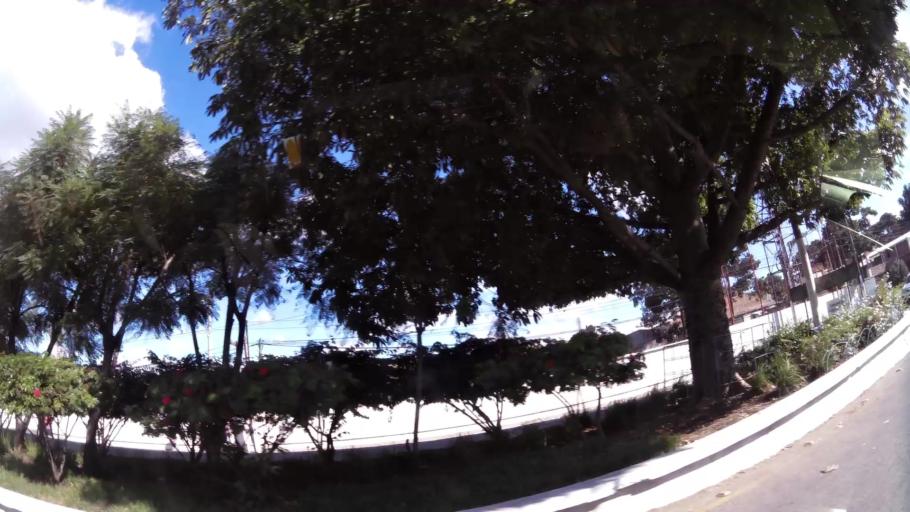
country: GT
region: Guatemala
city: Villa Nueva
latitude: 14.5314
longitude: -90.5862
